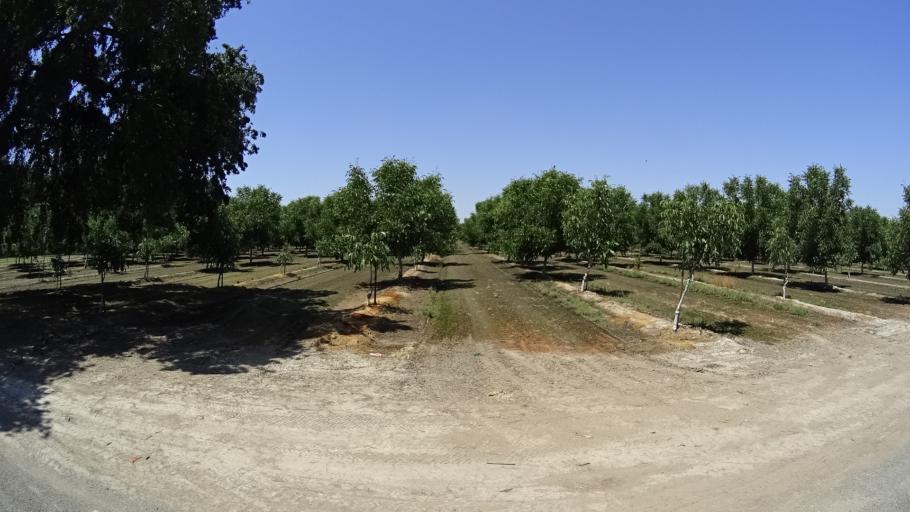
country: US
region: California
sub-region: Fresno County
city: Laton
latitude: 36.4130
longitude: -119.6864
